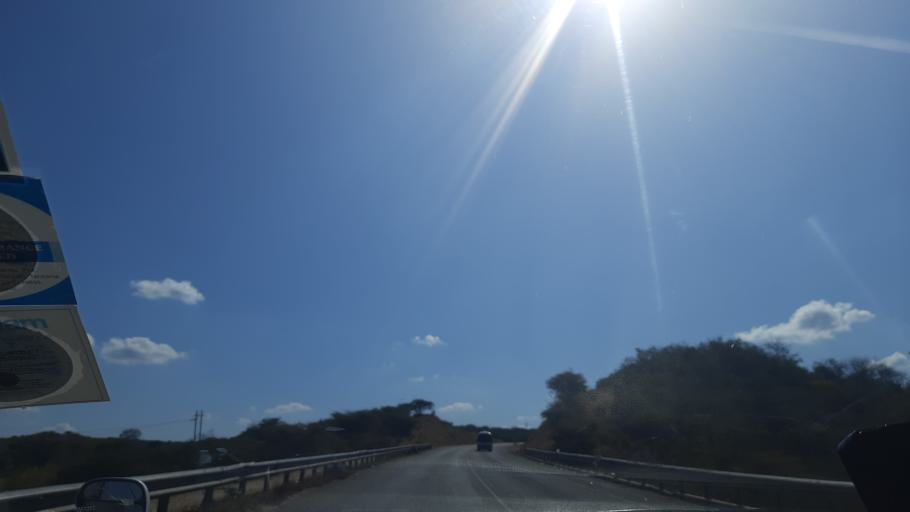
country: TZ
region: Singida
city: Kilimatinde
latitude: -5.7817
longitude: 34.8852
